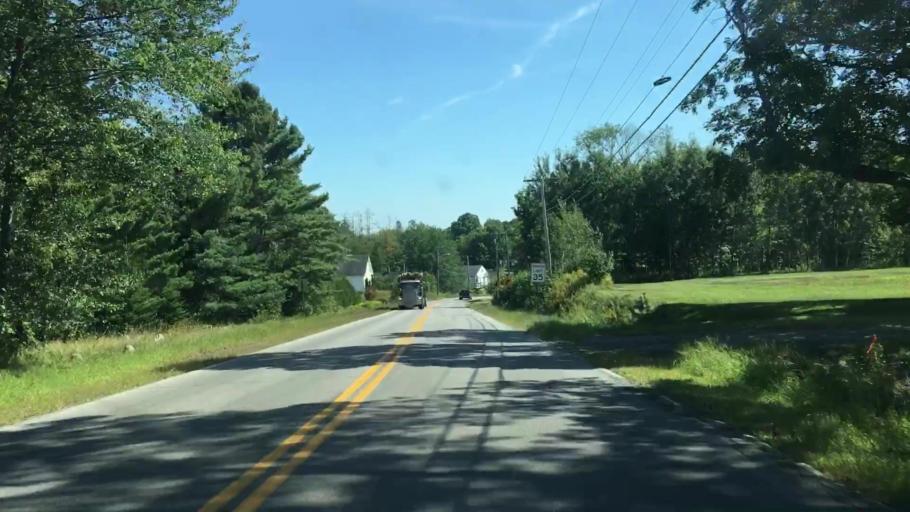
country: US
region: Maine
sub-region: Penobscot County
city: Bradford
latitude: 45.1702
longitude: -68.8487
